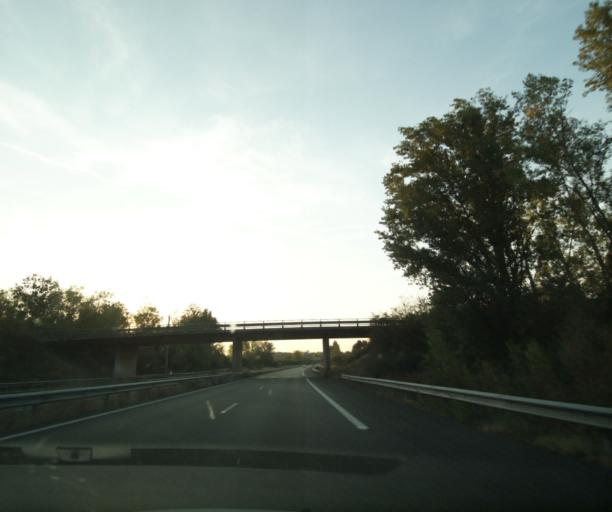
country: FR
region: Aquitaine
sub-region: Departement du Lot-et-Garonne
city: Fourques-sur-Garonne
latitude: 44.4303
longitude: 0.1359
